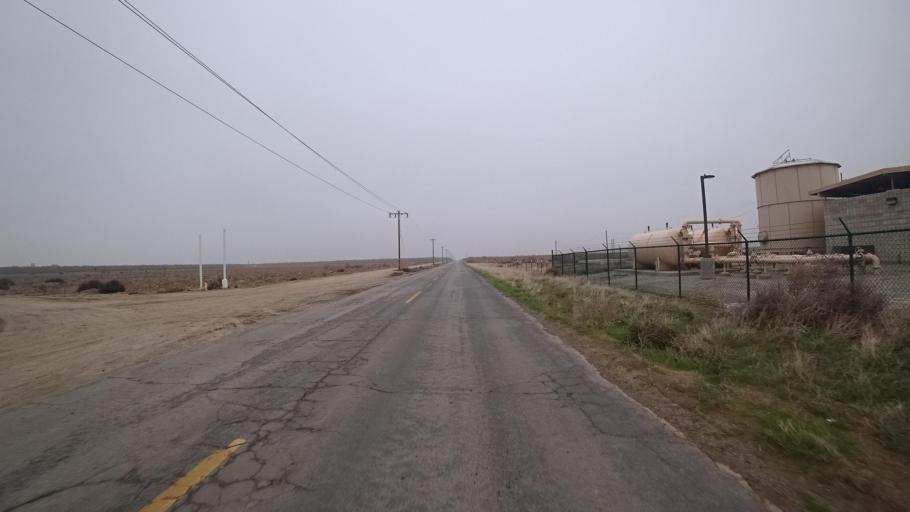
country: US
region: California
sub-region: Kern County
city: Wasco
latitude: 35.6169
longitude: -119.5091
